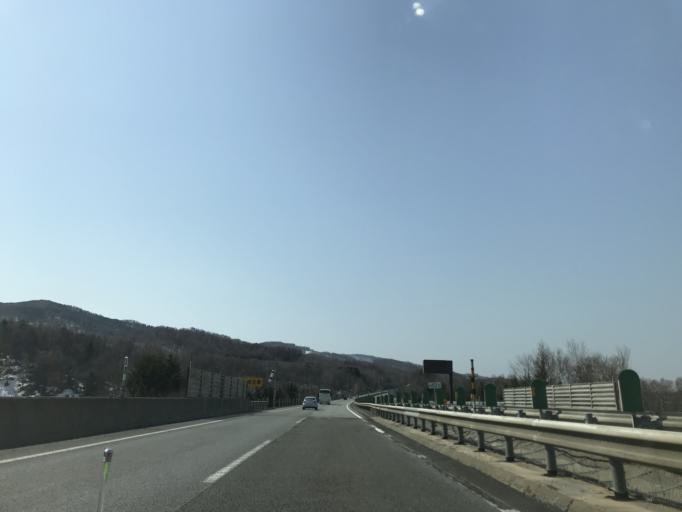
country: JP
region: Hokkaido
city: Bibai
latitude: 43.3279
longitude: 141.8880
